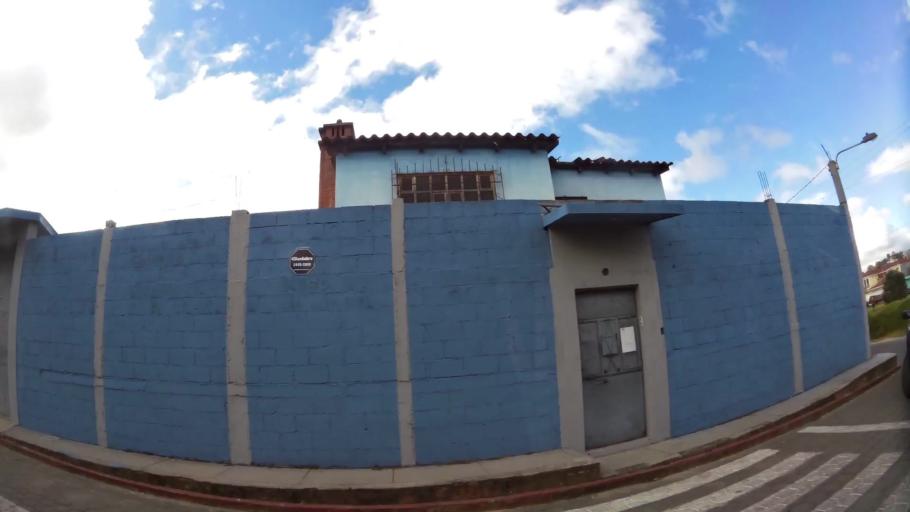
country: GT
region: Quetzaltenango
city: Salcaja
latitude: 14.8771
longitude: -91.4573
